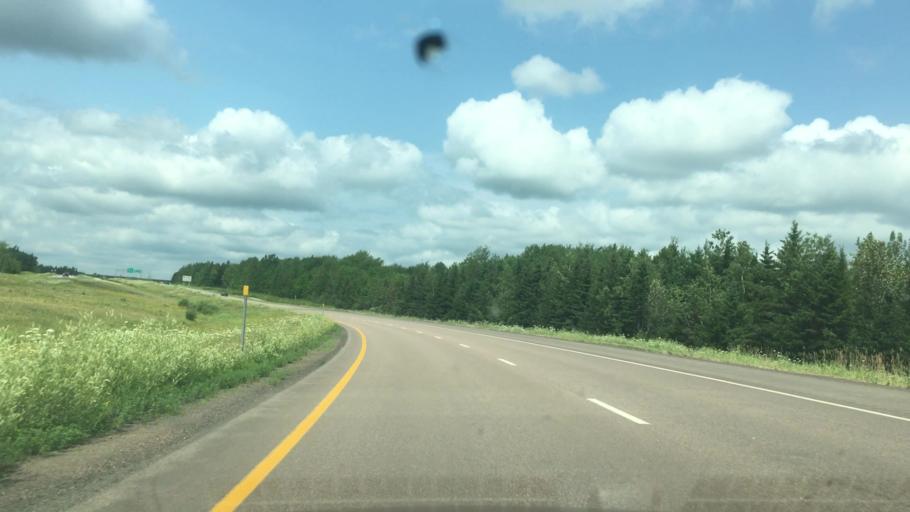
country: CA
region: New Brunswick
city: Dieppe
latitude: 46.0927
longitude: -64.5973
